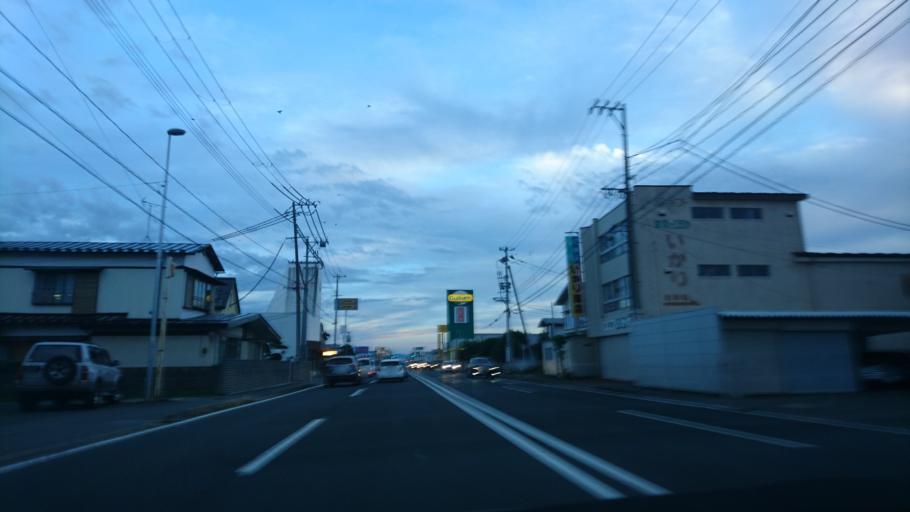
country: JP
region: Iwate
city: Morioka-shi
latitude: 39.6652
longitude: 141.1588
